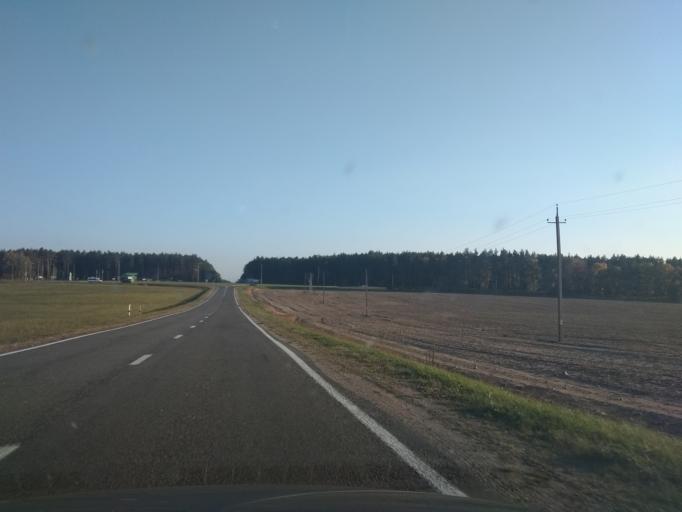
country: BY
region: Grodnenskaya
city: Vawkavysk
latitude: 53.1479
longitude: 24.5022
